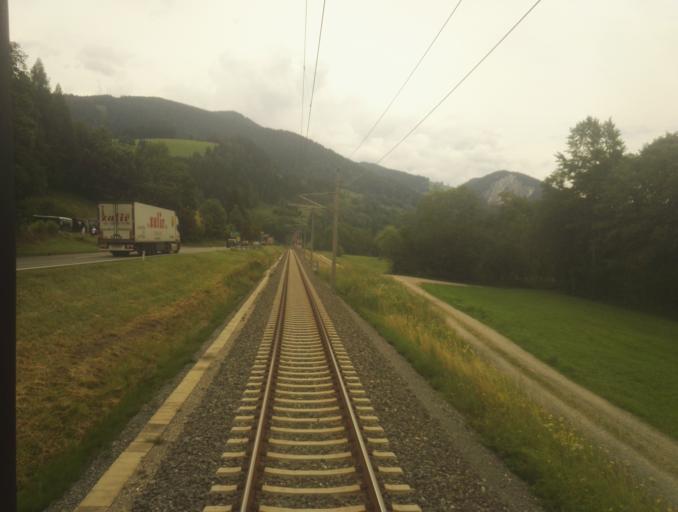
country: AT
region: Salzburg
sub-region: Politischer Bezirk Sankt Johann im Pongau
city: Forstau
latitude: 47.4022
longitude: 13.5549
